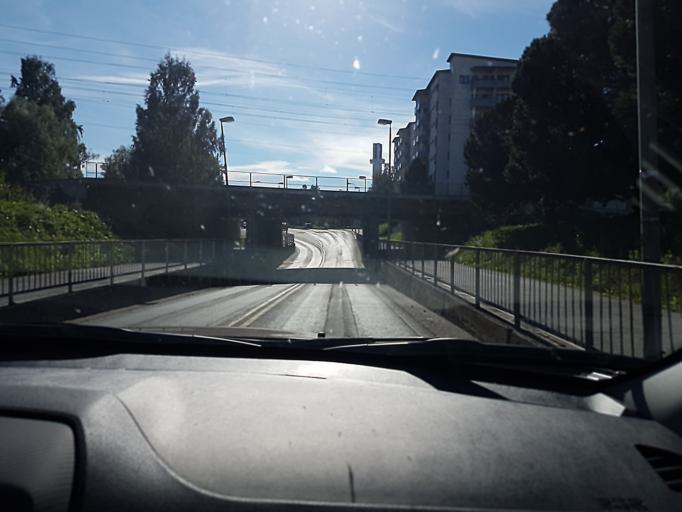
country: FI
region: Southern Ostrobothnia
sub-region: Seinaejoki
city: Seinaejoki
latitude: 62.7885
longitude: 22.8530
